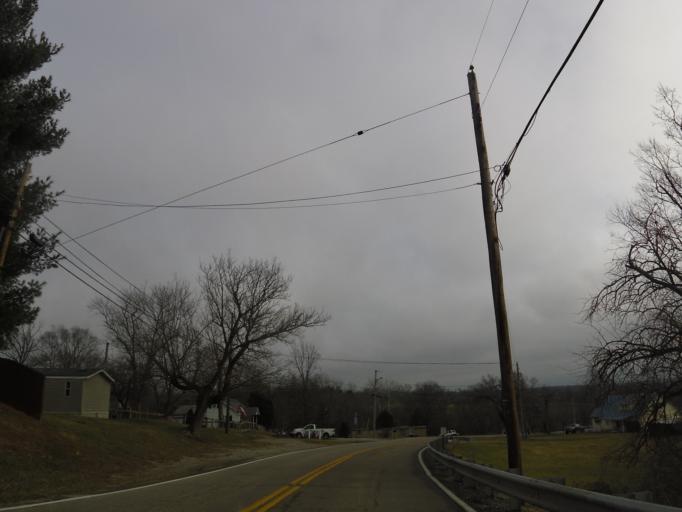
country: US
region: Kentucky
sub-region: Trimble County
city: Bedford
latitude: 38.5925
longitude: -85.3164
